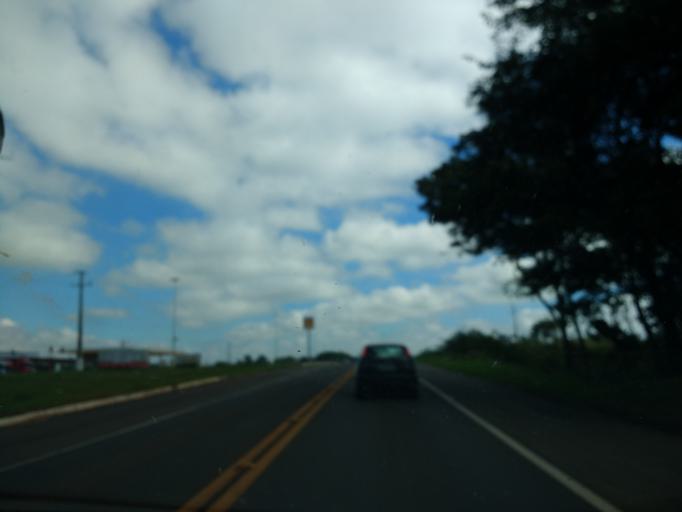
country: BR
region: Parana
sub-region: Cruzeiro Do Oeste
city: Cruzeiro do Oeste
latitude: -23.7649
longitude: -53.1290
